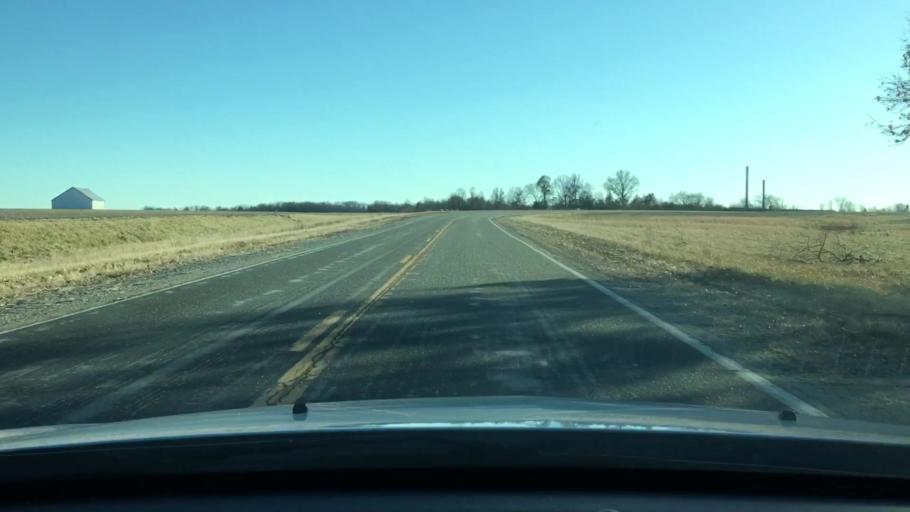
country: US
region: Missouri
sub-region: Audrain County
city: Mexico
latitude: 39.2129
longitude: -91.8528
